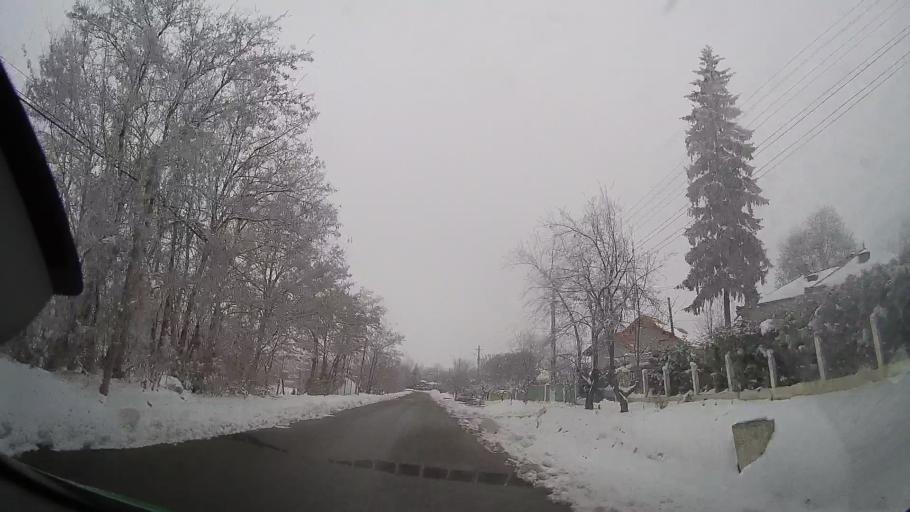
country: RO
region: Neamt
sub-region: Comuna Icusesti
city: Balusesti
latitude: 46.8598
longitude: 27.0205
